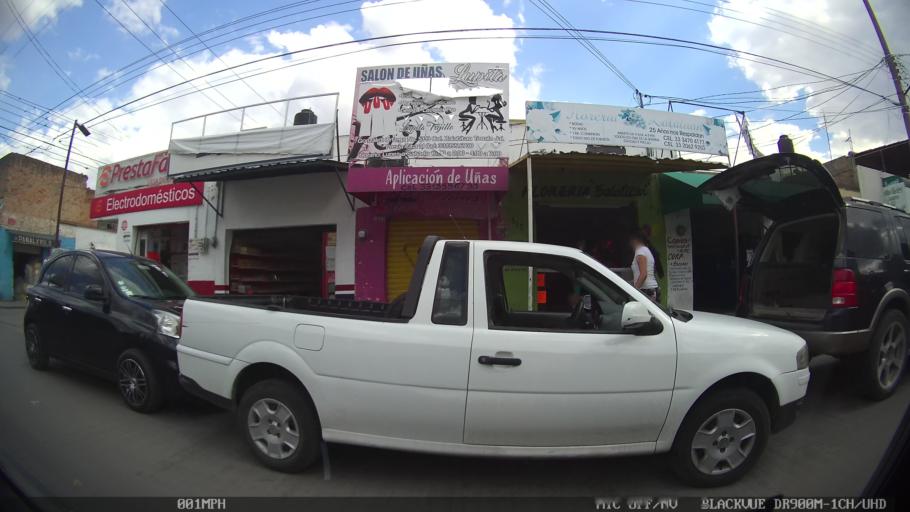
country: MX
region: Jalisco
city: Tlaquepaque
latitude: 20.6568
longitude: -103.2620
